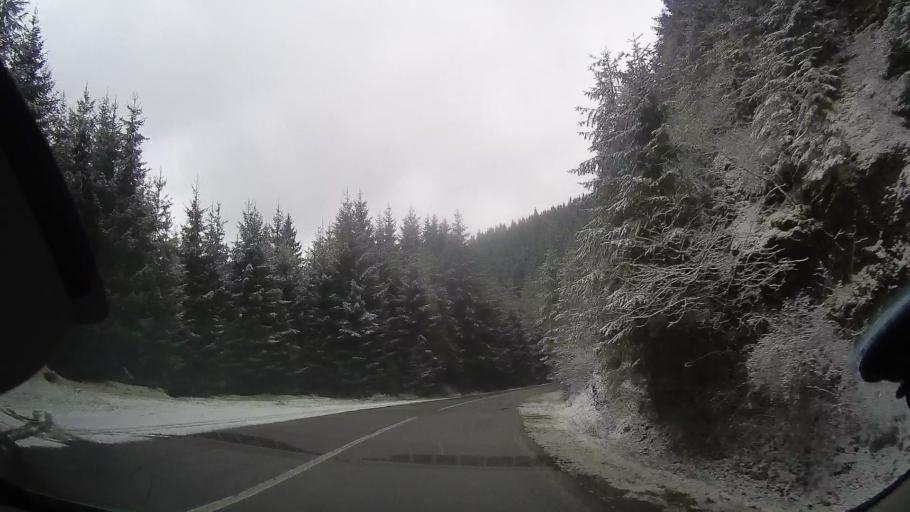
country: RO
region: Cluj
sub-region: Comuna Belis
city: Belis
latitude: 46.6573
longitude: 23.0557
